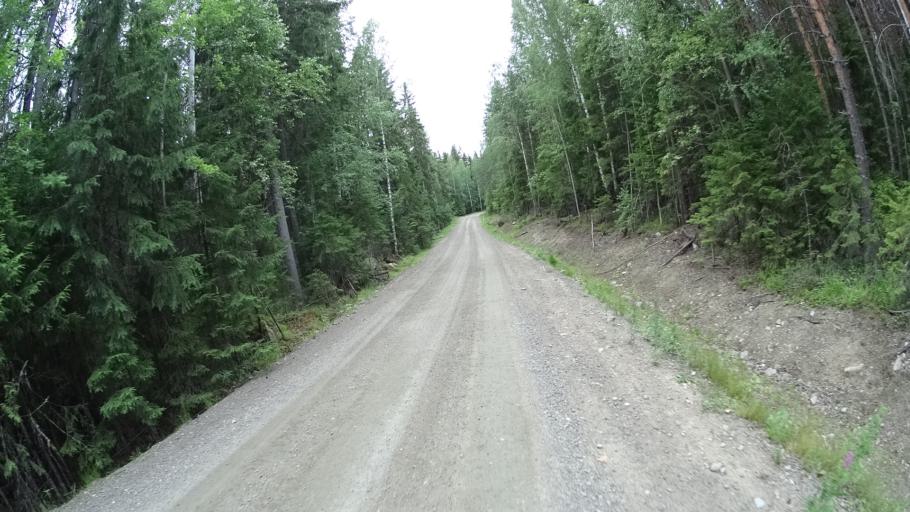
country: FI
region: Southern Savonia
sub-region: Mikkeli
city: Maentyharju
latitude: 61.1544
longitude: 26.8926
